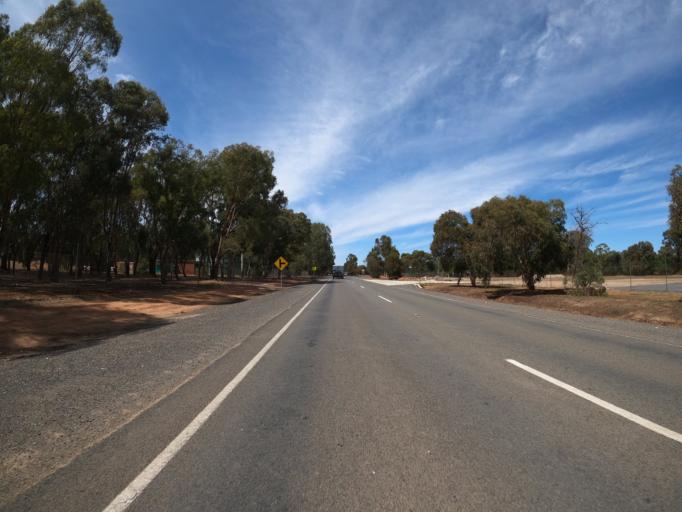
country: AU
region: Victoria
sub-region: Moira
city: Yarrawonga
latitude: -36.0349
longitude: 145.9955
